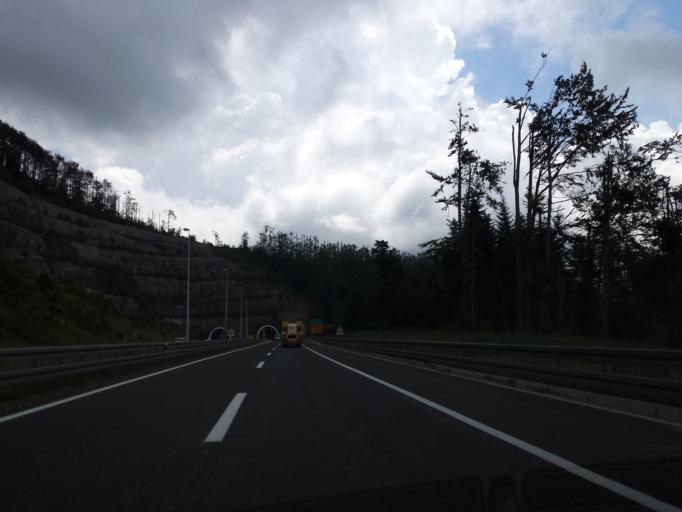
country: HR
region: Primorsko-Goranska
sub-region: Grad Delnice
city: Delnice
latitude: 45.3166
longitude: 14.7148
